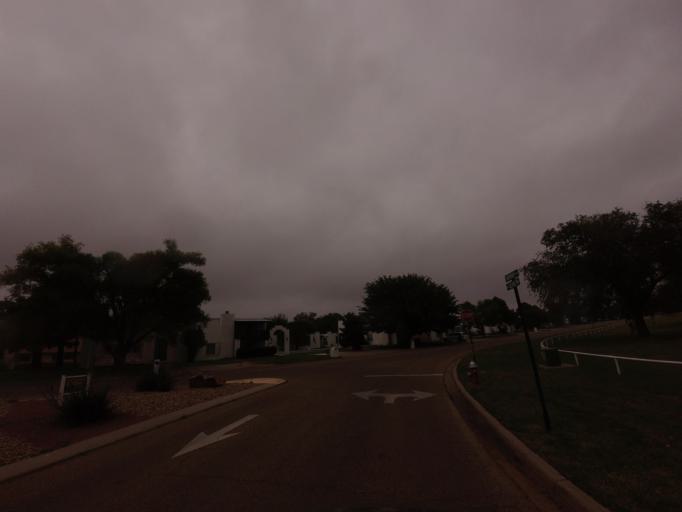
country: US
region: New Mexico
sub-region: Curry County
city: Clovis
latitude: 34.4392
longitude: -103.1941
